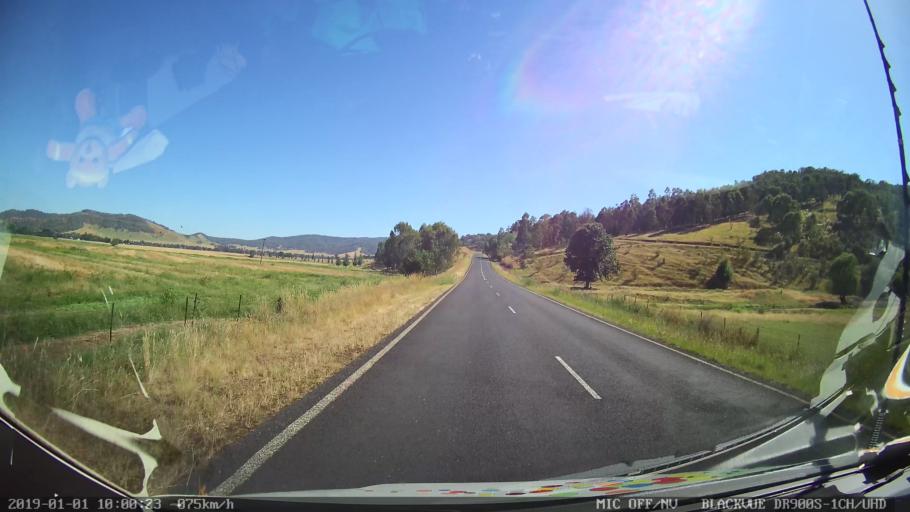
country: AU
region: New South Wales
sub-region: Snowy River
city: Jindabyne
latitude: -36.2028
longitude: 148.1013
